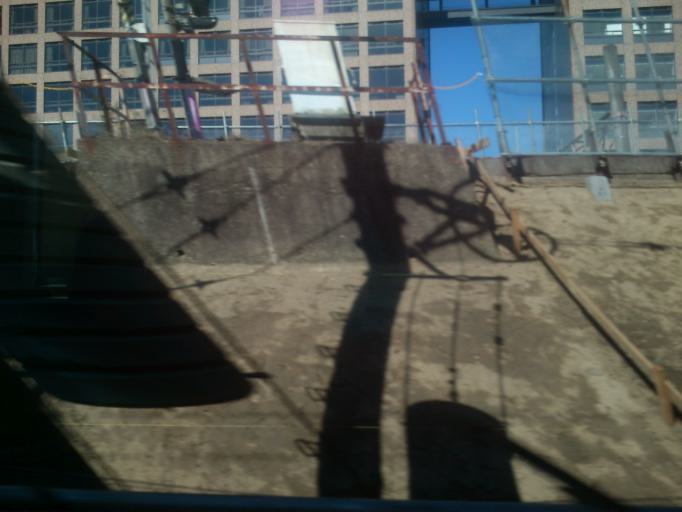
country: JP
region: Osaka
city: Takatsuki
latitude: 34.8544
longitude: 135.6230
